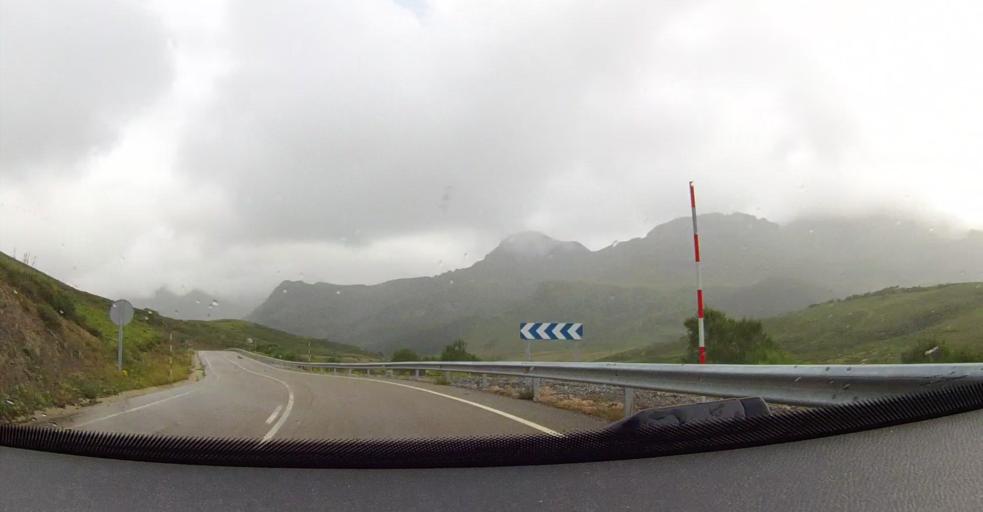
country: ES
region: Castille and Leon
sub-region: Provincia de Leon
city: Marana
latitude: 43.0820
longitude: -5.2150
